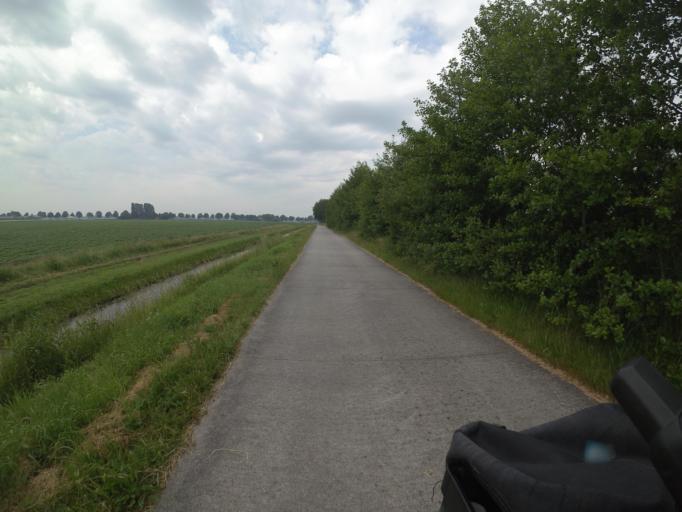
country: NL
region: Drenthe
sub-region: Gemeente Assen
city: Assen
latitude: 53.0002
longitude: 6.4690
